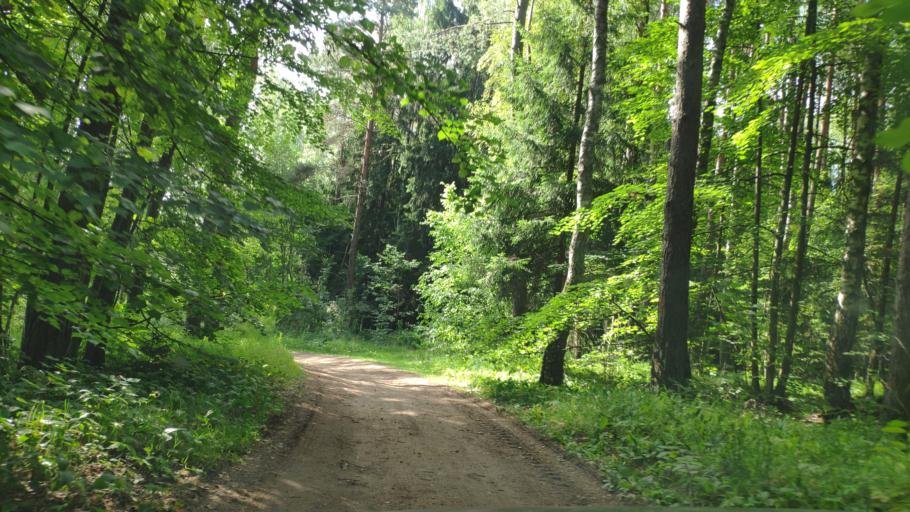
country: BY
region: Minsk
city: Zaslawye
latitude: 53.9722
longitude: 27.2930
